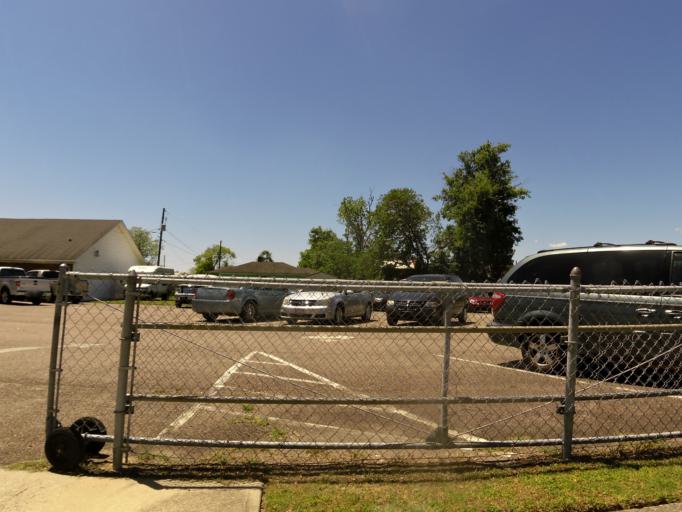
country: US
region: Georgia
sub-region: Richmond County
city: Augusta
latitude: 33.4655
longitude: -81.9742
